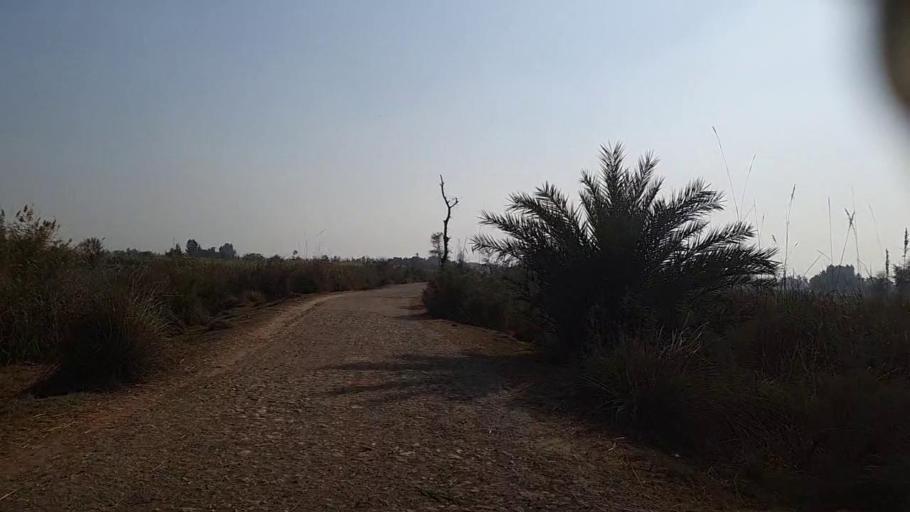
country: PK
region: Sindh
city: Mirpur Mathelo
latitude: 27.9006
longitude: 69.6067
